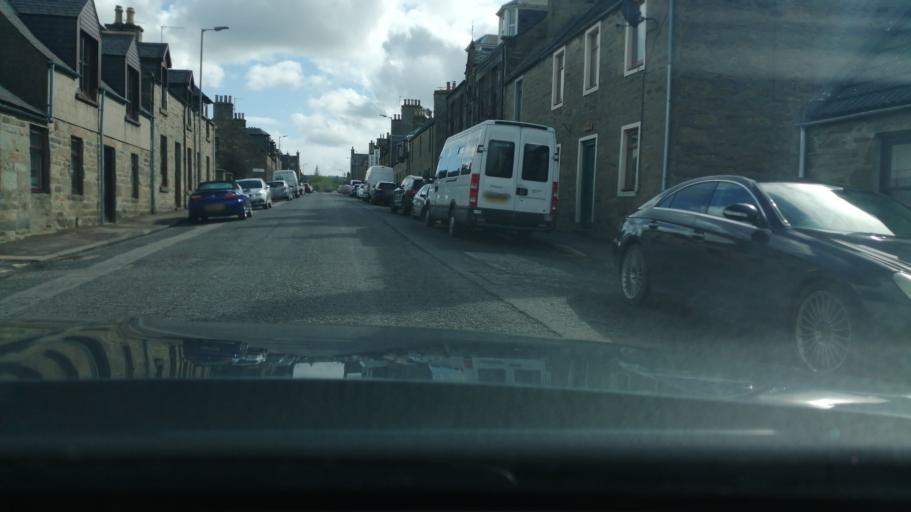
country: GB
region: Scotland
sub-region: Moray
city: Keith
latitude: 57.5403
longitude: -2.9522
